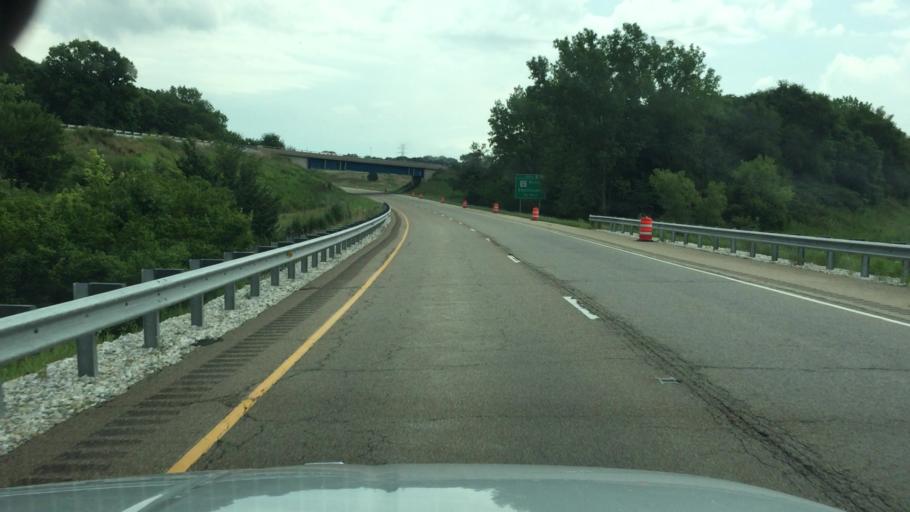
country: US
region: Illinois
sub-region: Peoria County
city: Bellevue
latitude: 40.7427
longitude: -89.6741
